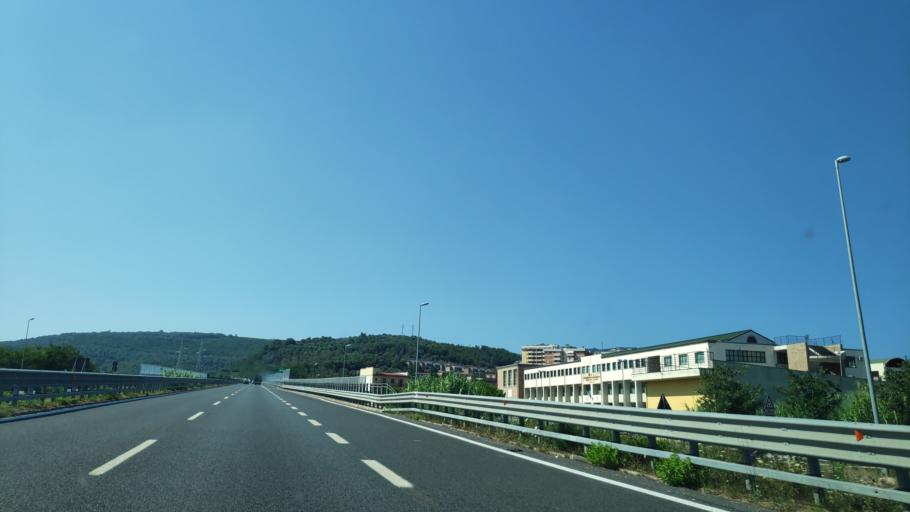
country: IT
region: Calabria
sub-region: Provincia di Reggio Calabria
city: Seminara
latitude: 38.3667
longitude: 15.8652
